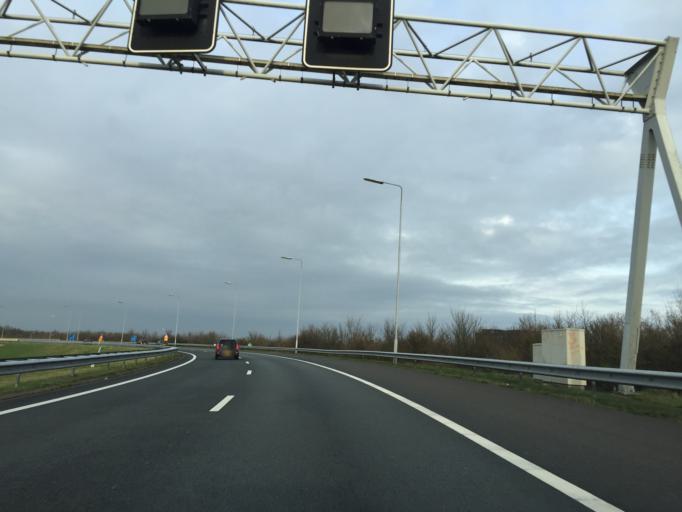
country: NL
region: Utrecht
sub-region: Gemeente Nieuwegein
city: Nieuwegein
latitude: 52.0660
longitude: 5.0734
